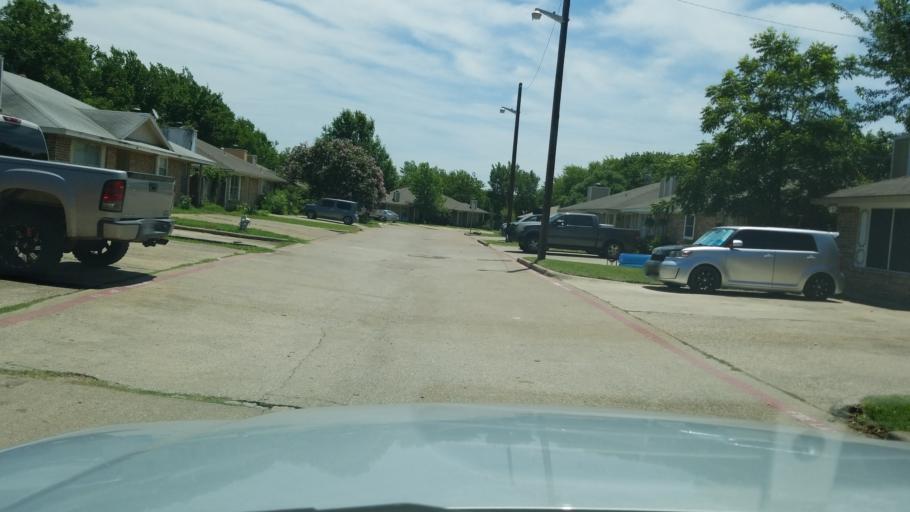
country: US
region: Texas
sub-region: Dallas County
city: Irving
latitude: 32.8046
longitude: -96.9239
